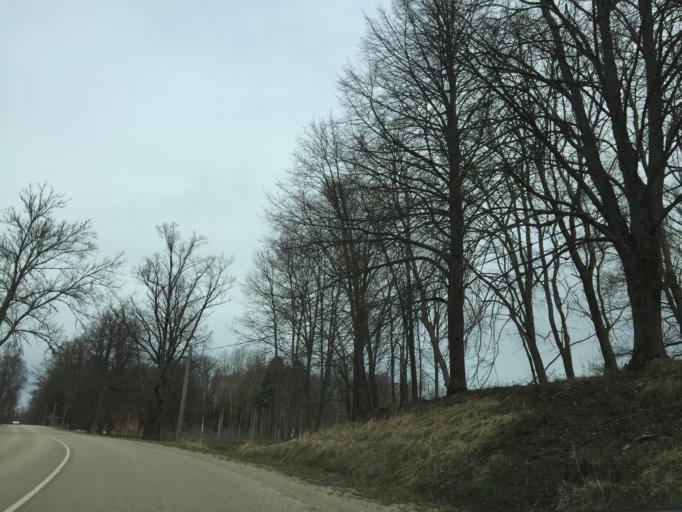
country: LV
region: Amatas Novads
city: Drabesi
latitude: 57.2544
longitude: 25.2779
